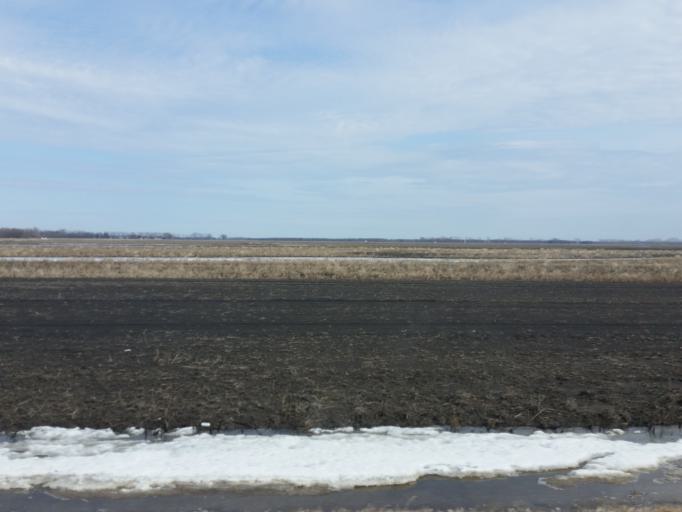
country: US
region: North Dakota
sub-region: Walsh County
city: Grafton
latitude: 48.4248
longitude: -97.2122
